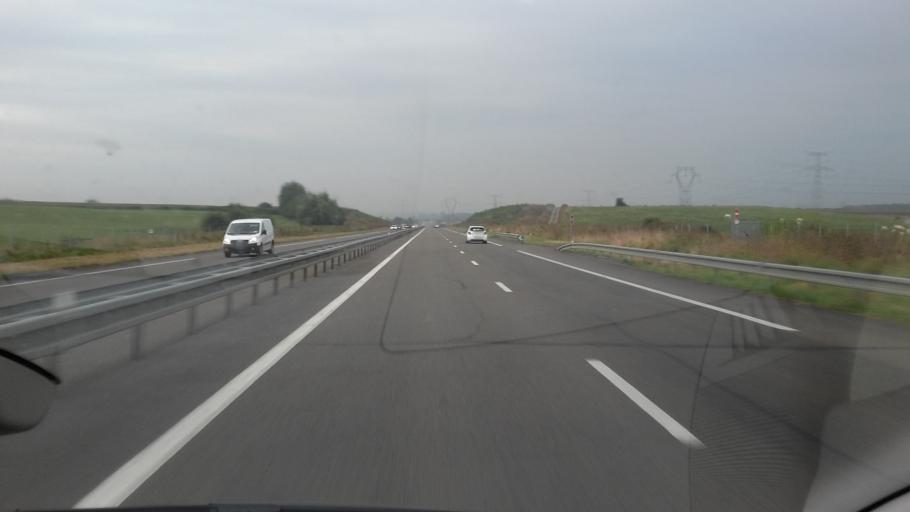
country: FR
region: Champagne-Ardenne
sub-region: Departement des Ardennes
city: Rethel
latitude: 49.5779
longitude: 4.4816
